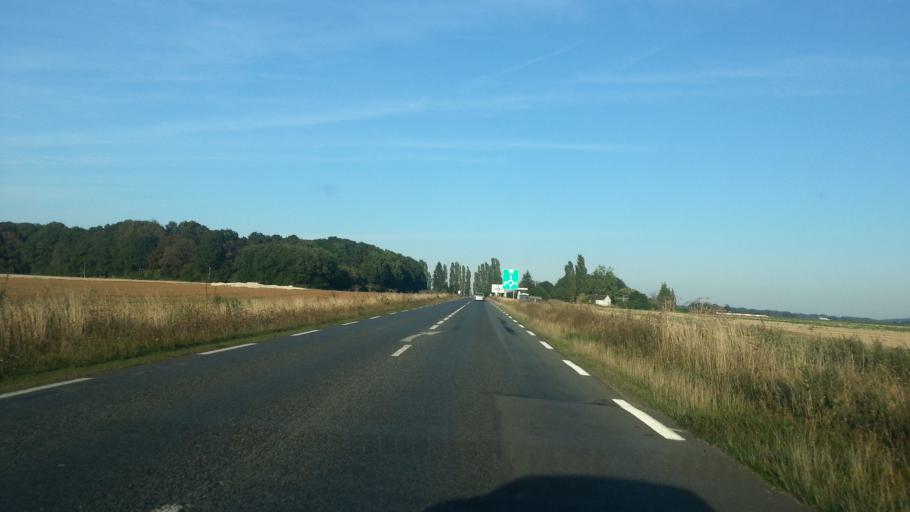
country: FR
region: Picardie
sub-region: Departement de l'Oise
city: Estrees-Saint-Denis
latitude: 49.4018
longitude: 2.6205
